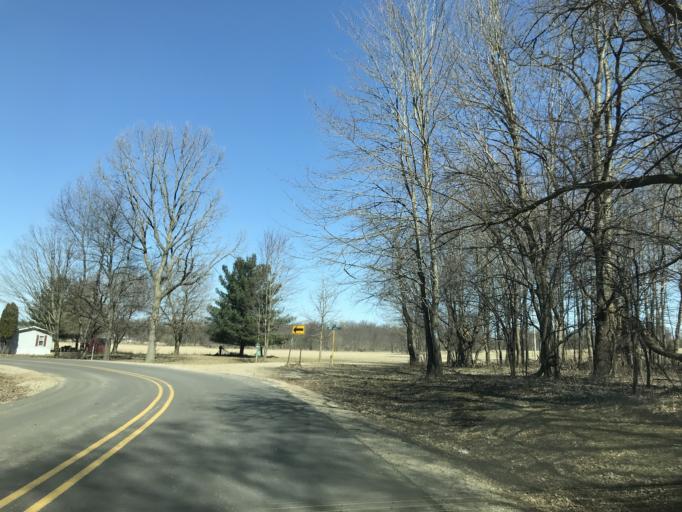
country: US
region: Michigan
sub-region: Hillsdale County
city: Jonesville
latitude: 41.9853
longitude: -84.6727
